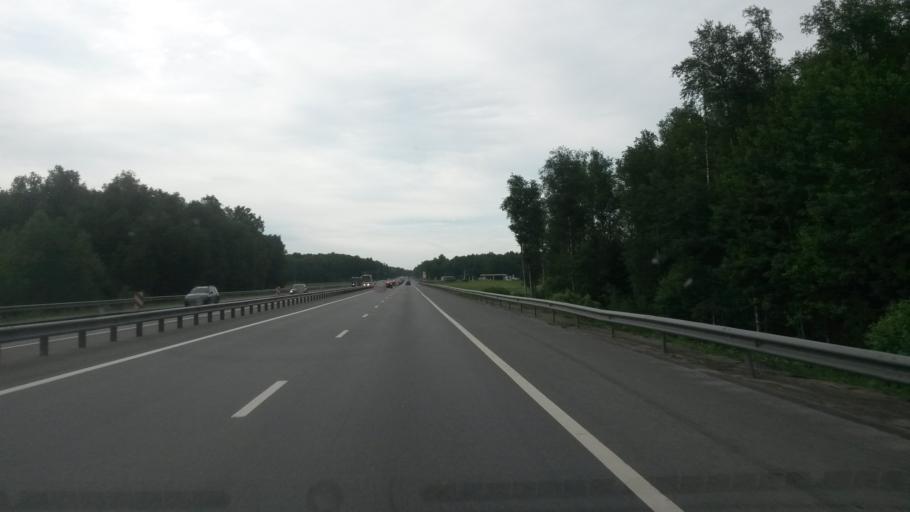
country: RU
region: Moskovskaya
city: Ashukino
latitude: 56.1502
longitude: 38.0110
